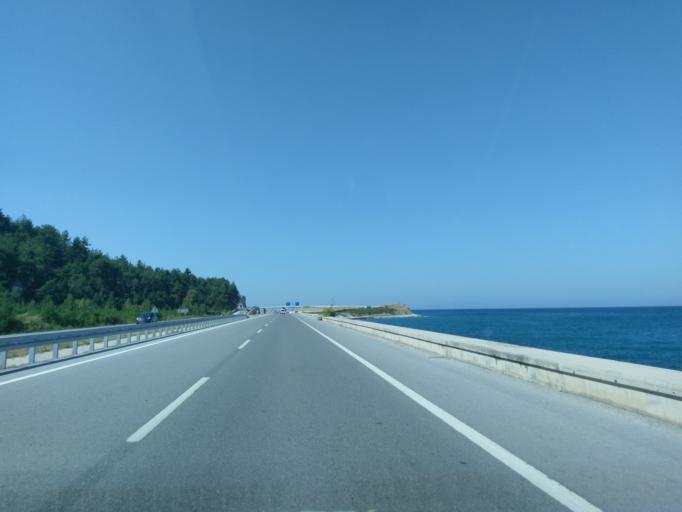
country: TR
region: Samsun
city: Yakakent
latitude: 41.6769
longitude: 35.4195
